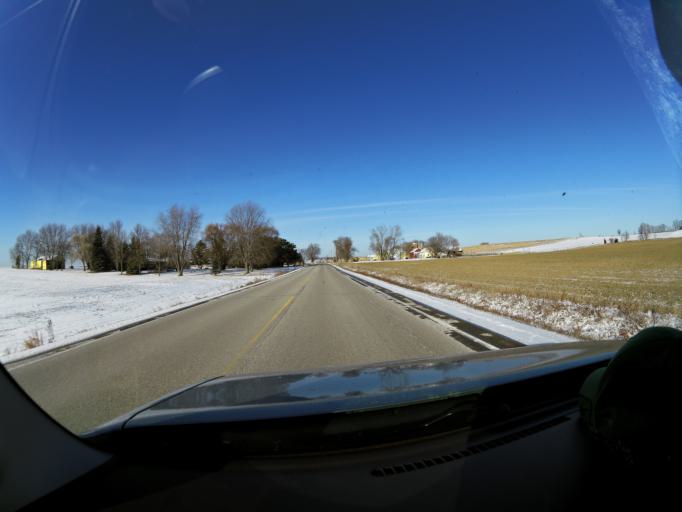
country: US
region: Minnesota
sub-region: Washington County
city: Cottage Grove
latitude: 44.8270
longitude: -92.8628
